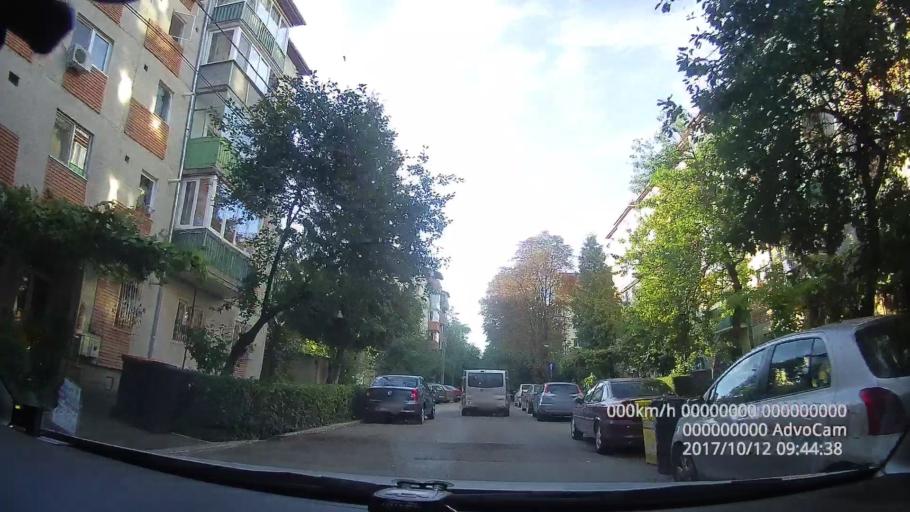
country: RO
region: Timis
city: Timisoara
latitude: 45.7729
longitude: 21.2307
